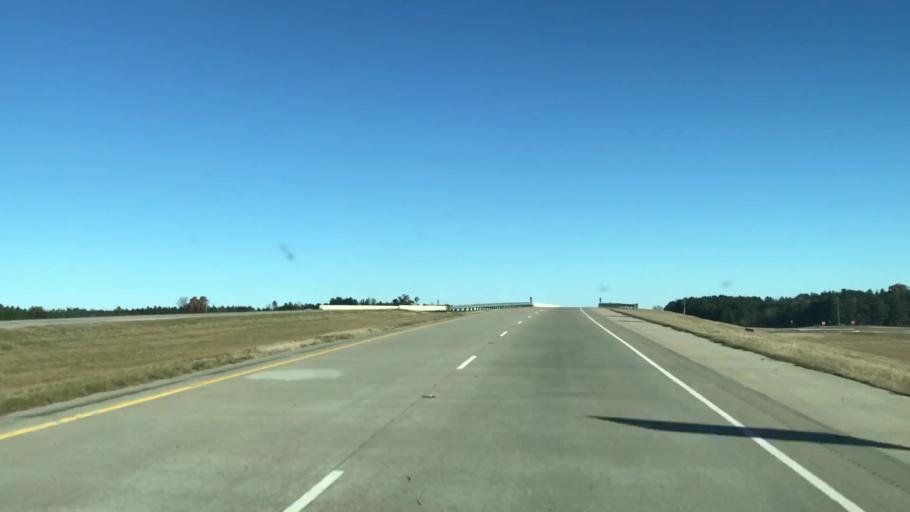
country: US
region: Louisiana
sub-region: Caddo Parish
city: Oil City
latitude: 32.8127
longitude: -93.8837
